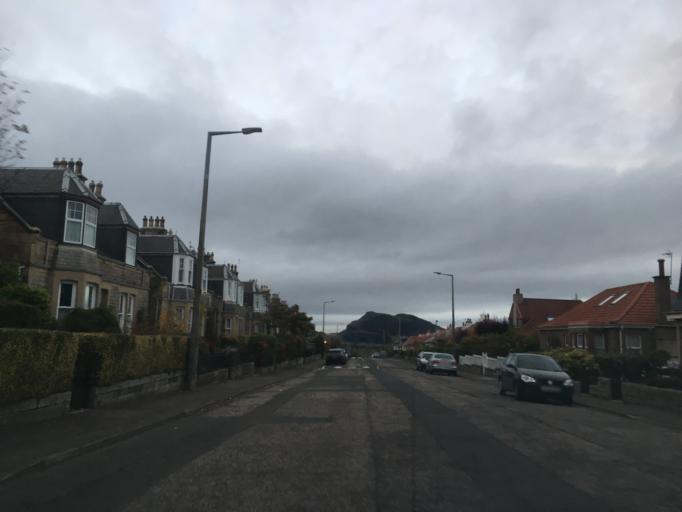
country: GB
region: Scotland
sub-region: Midlothian
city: Loanhead
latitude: 55.9127
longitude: -3.1685
